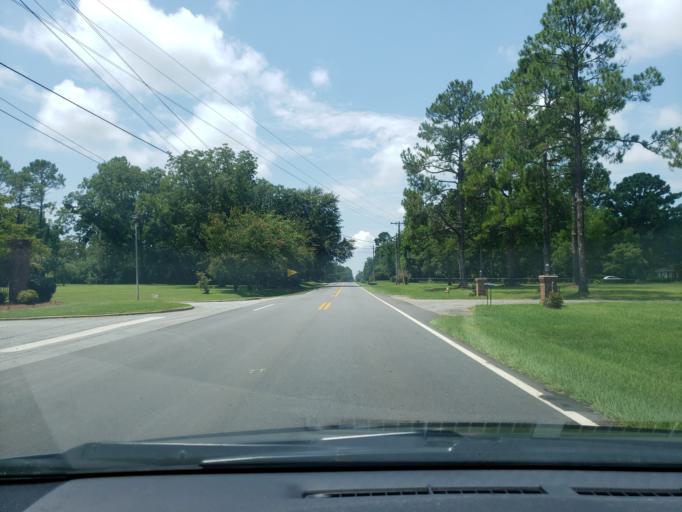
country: US
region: Georgia
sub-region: Dougherty County
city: Albany
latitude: 31.6131
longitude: -84.2686
